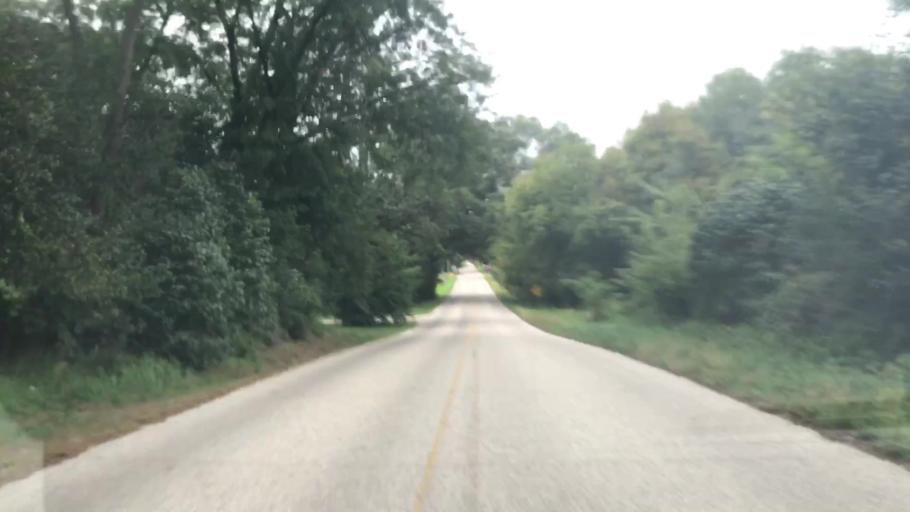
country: US
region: Wisconsin
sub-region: Waukesha County
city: North Prairie
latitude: 42.9152
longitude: -88.4377
